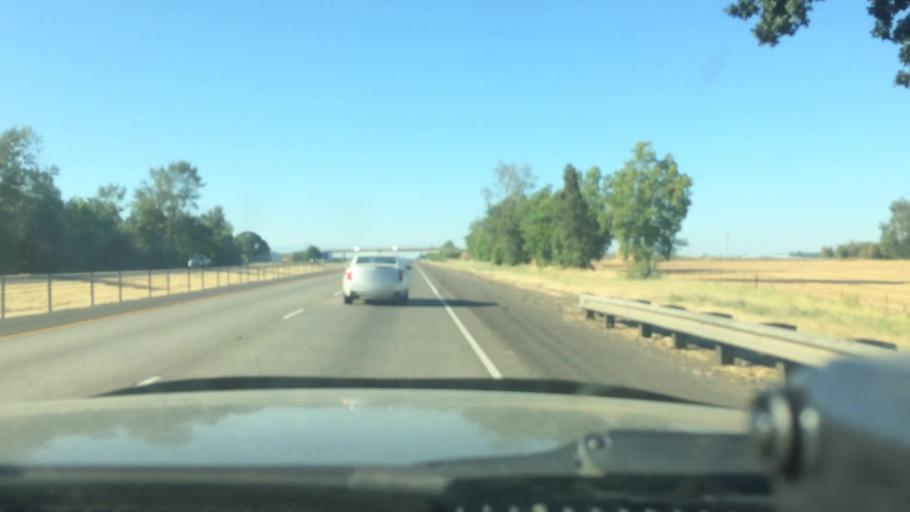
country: US
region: Oregon
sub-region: Linn County
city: Albany
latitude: 44.5895
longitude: -123.0622
